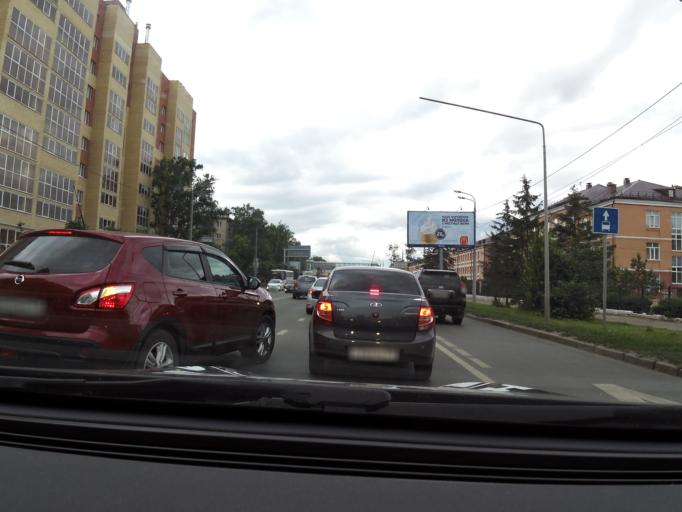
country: RU
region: Tatarstan
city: Staroye Arakchino
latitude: 55.8255
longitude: 49.0371
